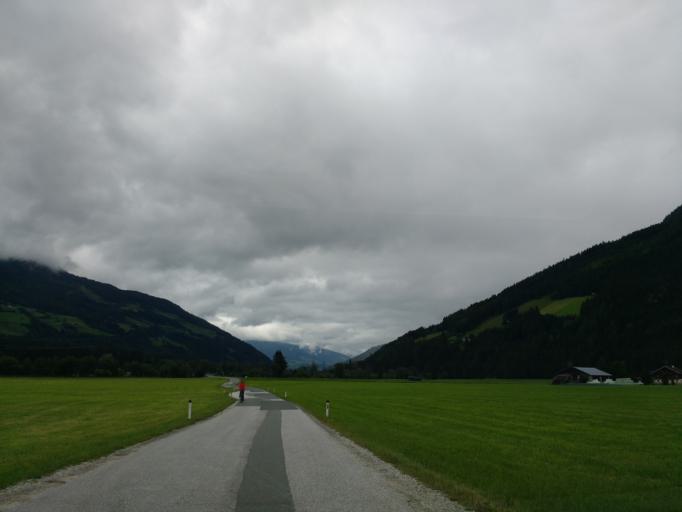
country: AT
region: Salzburg
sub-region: Politischer Bezirk Zell am See
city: Neukirchen am Grossvenediger
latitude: 47.2402
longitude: 12.2567
